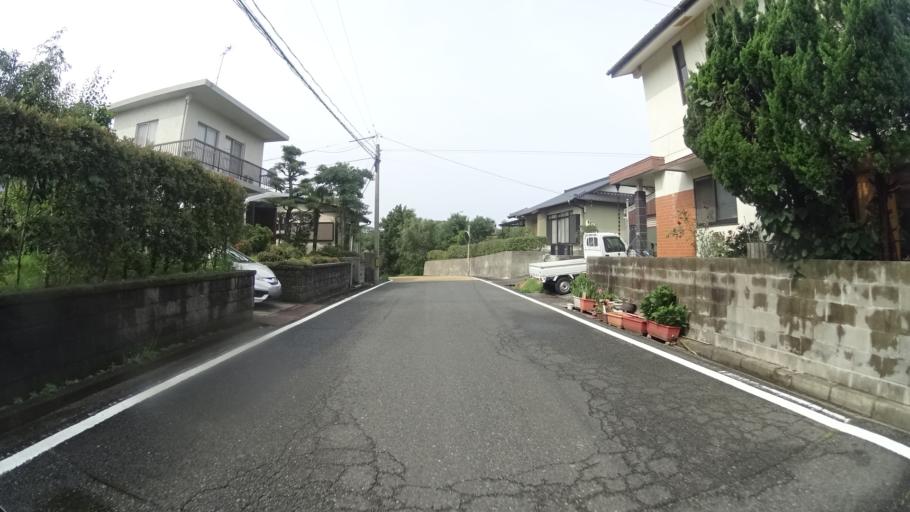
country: JP
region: Yamaguchi
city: Shimonoseki
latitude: 34.0903
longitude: 130.8821
